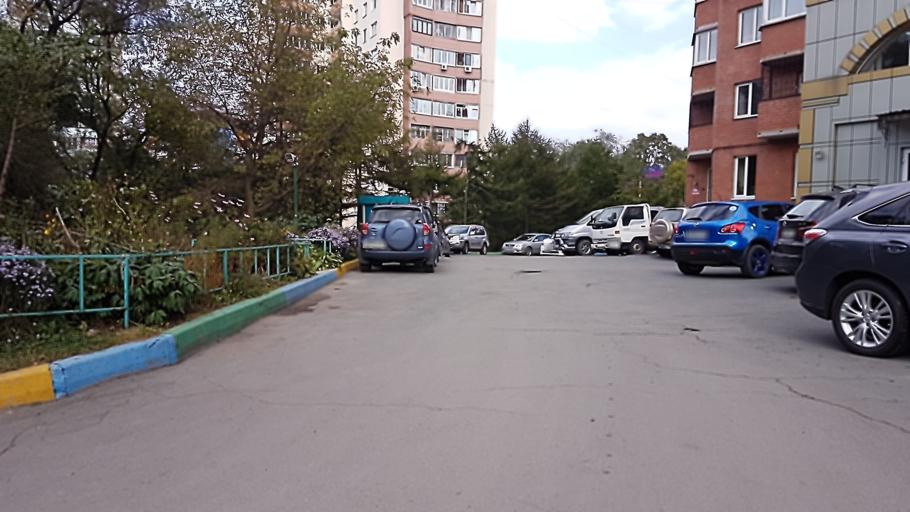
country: RU
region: Primorskiy
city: Vladivostok
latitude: 43.1294
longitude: 131.9095
